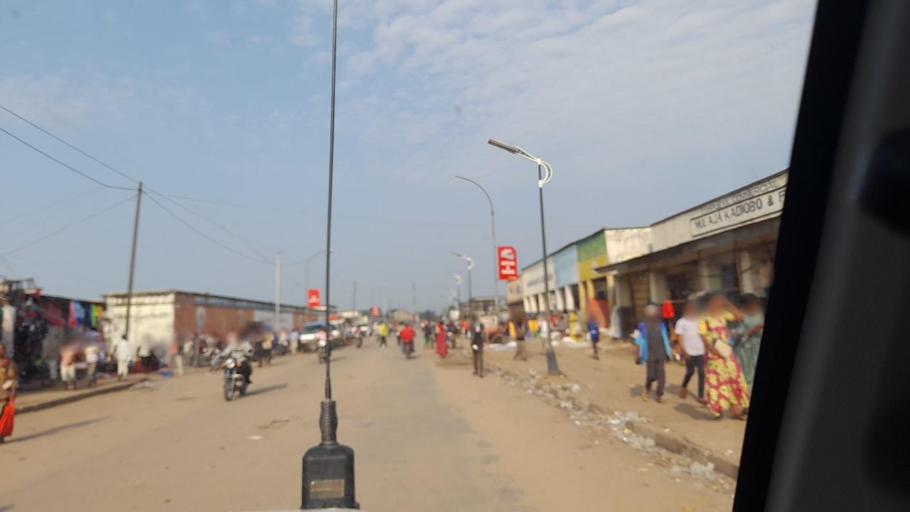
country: CD
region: Kasai-Occidental
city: Kananga
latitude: -5.8949
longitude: 22.3966
